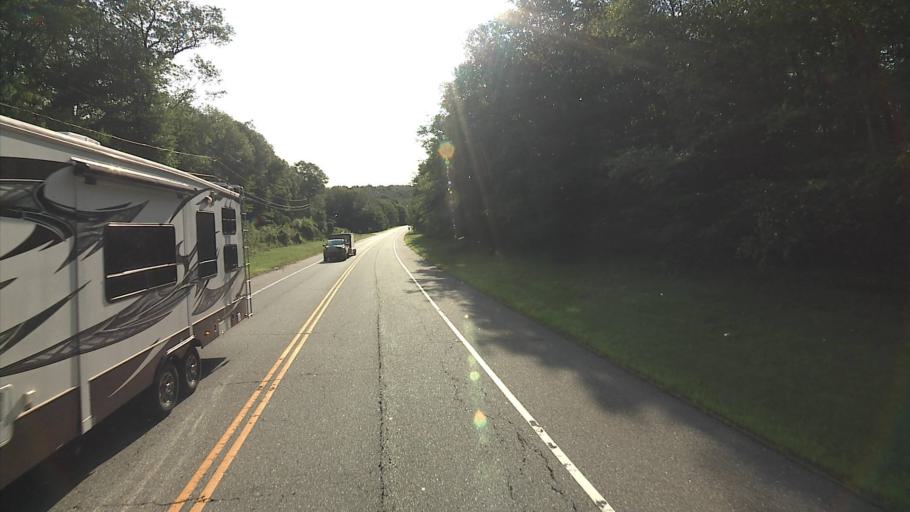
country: US
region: Connecticut
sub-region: New London County
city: Preston City
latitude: 41.4670
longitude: -71.9207
